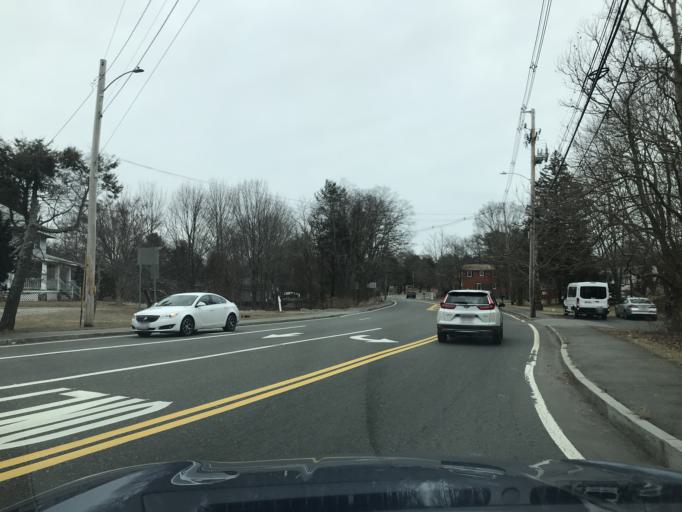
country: US
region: Massachusetts
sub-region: Essex County
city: Lynnfield
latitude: 42.5125
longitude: -71.0277
